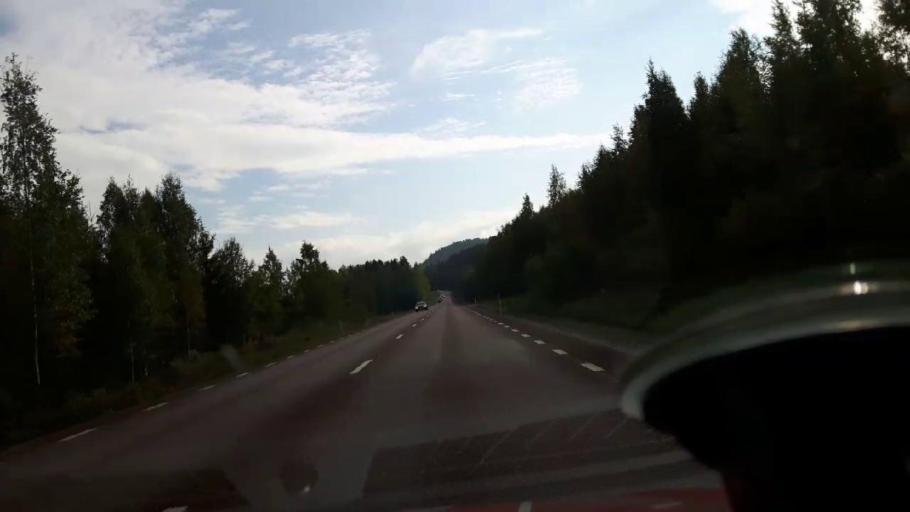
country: SE
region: Gaevleborg
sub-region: Bollnas Kommun
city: Kilafors
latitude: 61.2108
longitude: 16.7400
